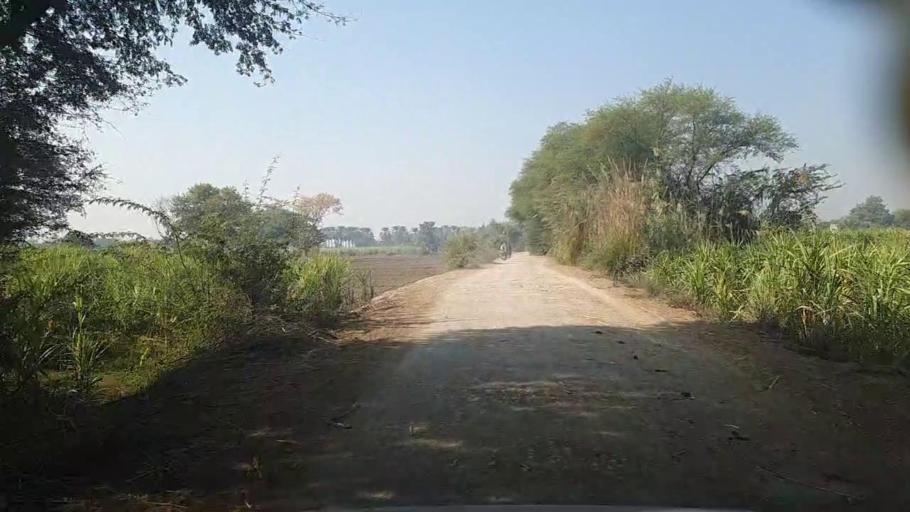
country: PK
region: Sindh
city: Kandiari
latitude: 26.9942
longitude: 68.4769
